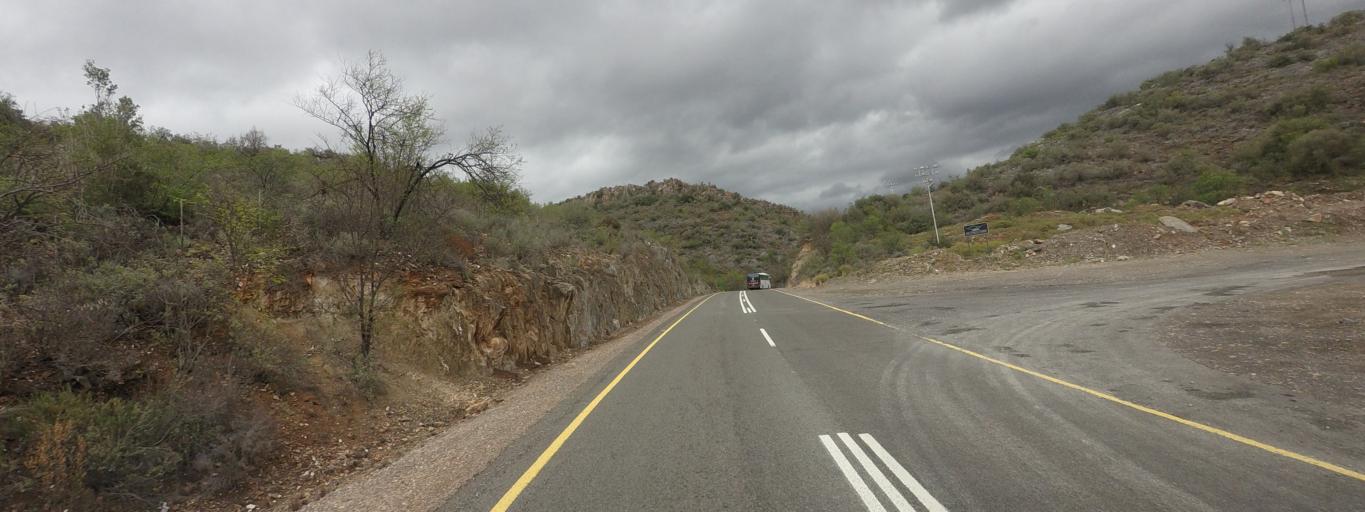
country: ZA
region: Western Cape
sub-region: Eden District Municipality
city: Oudtshoorn
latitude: -33.4167
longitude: 22.2371
